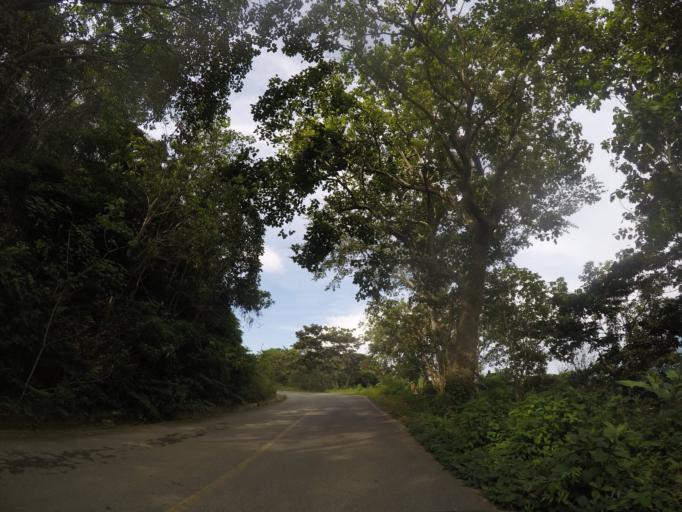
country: MX
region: Oaxaca
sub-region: San Pedro Pochutla
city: Los Naranjos Esquipulas
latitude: 15.9542
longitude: -96.4498
